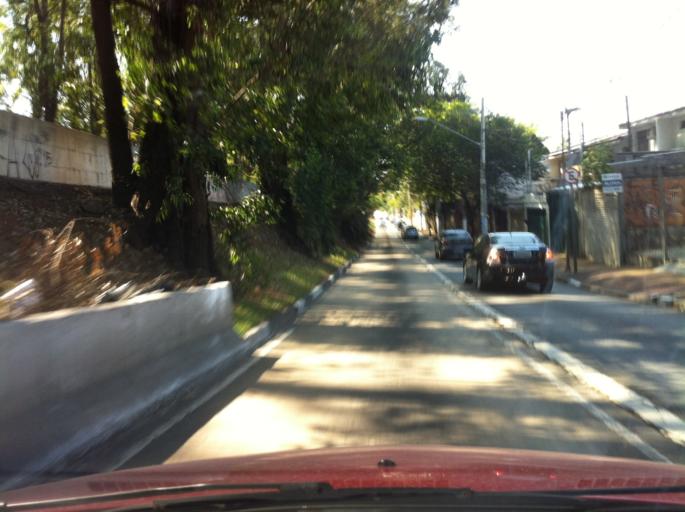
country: BR
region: Sao Paulo
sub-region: Diadema
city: Diadema
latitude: -23.6324
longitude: -46.6893
